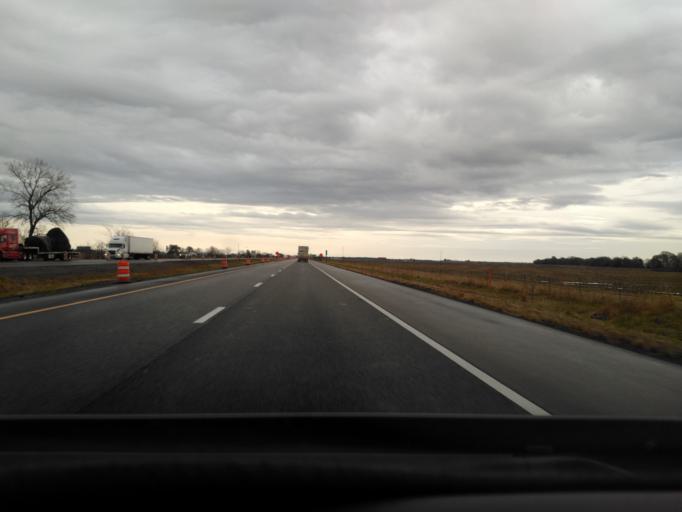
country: US
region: Illinois
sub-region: Bond County
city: Greenville
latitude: 38.8753
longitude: -89.3695
